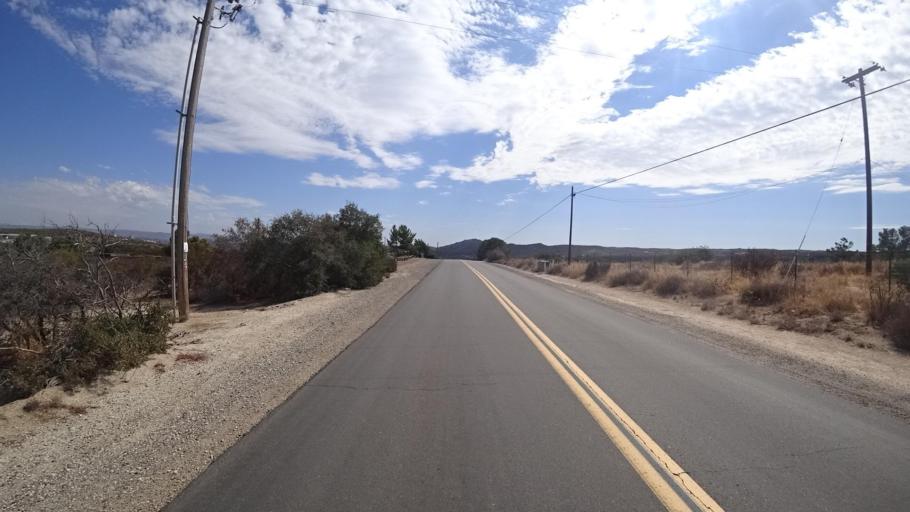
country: MX
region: Baja California
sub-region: Tecate
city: Cereso del Hongo
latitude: 32.6570
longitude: -116.2906
